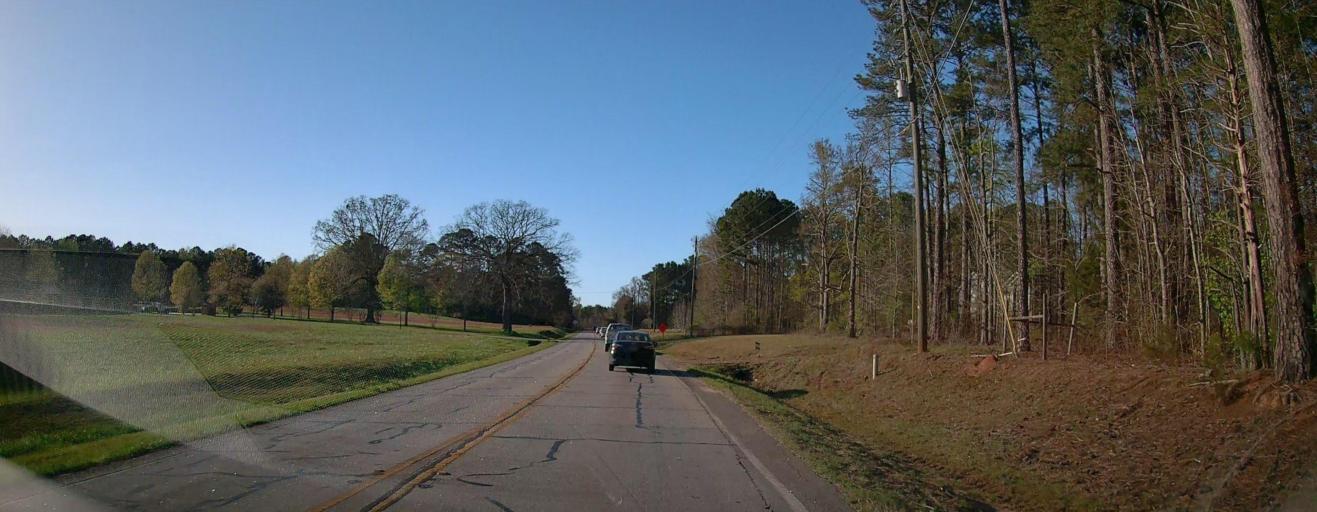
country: US
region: Georgia
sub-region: Newton County
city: Oakwood
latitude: 33.4576
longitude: -83.9042
